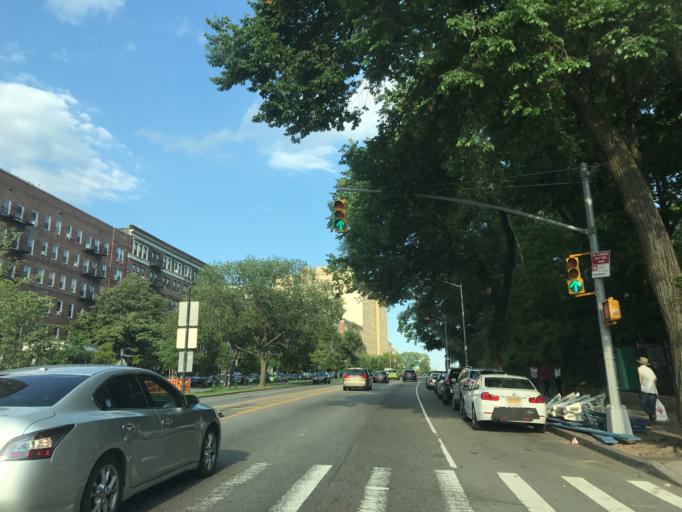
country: US
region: New York
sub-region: Kings County
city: Brooklyn
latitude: 40.6728
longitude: -73.9676
